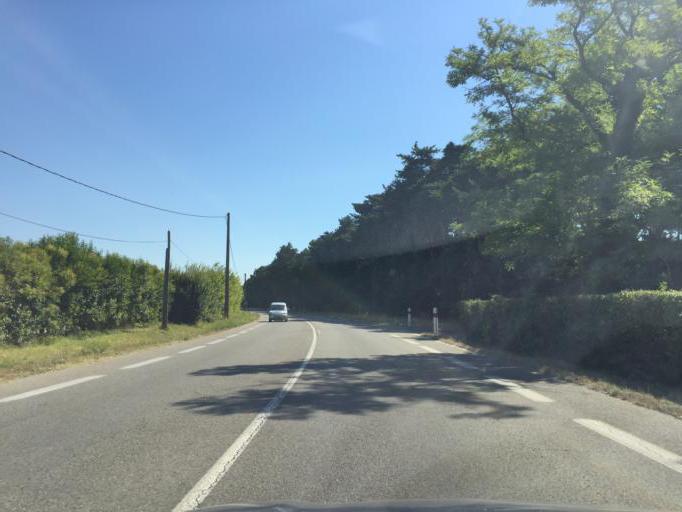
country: FR
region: Provence-Alpes-Cote d'Azur
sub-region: Departement du Vaucluse
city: Jonquerettes
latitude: 43.9628
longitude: 4.9512
